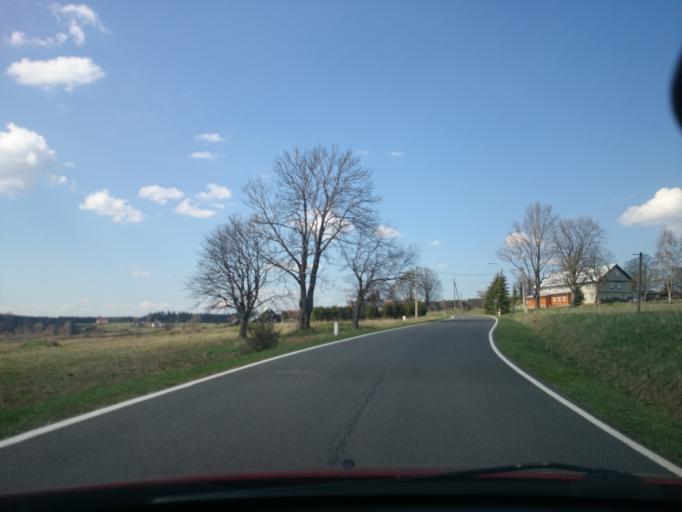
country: PL
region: Lower Silesian Voivodeship
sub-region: Powiat klodzki
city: Szczytna
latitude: 50.3071
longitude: 16.4504
